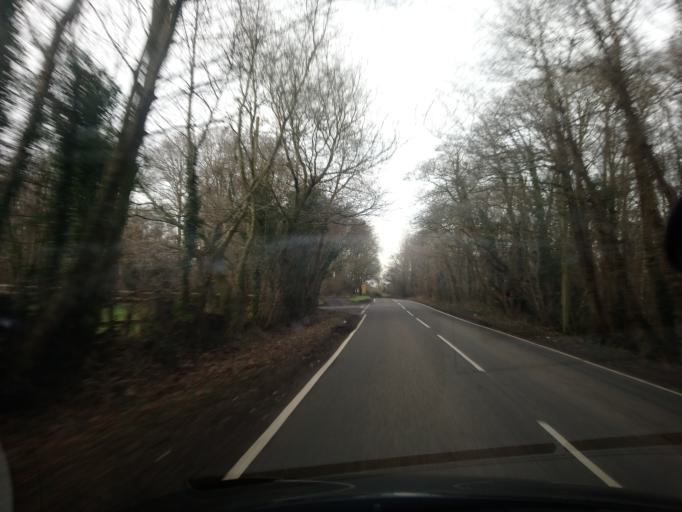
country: GB
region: England
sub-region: Shropshire
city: Prees
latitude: 52.9227
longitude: -2.6812
